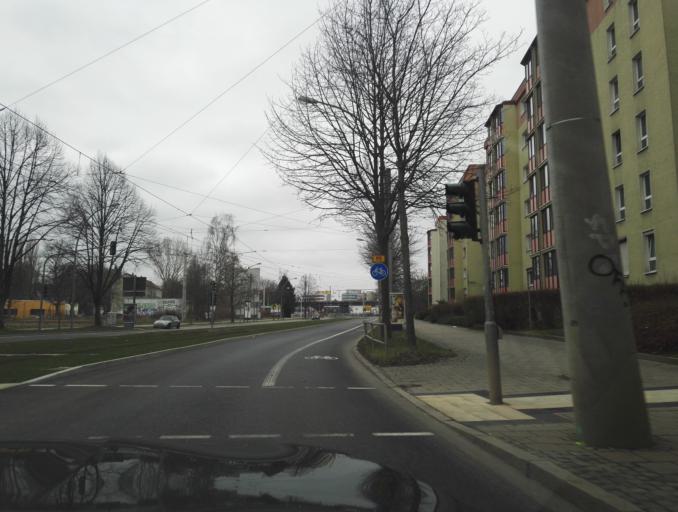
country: DE
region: Saxony
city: Chemnitz
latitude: 50.8283
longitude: 12.9206
